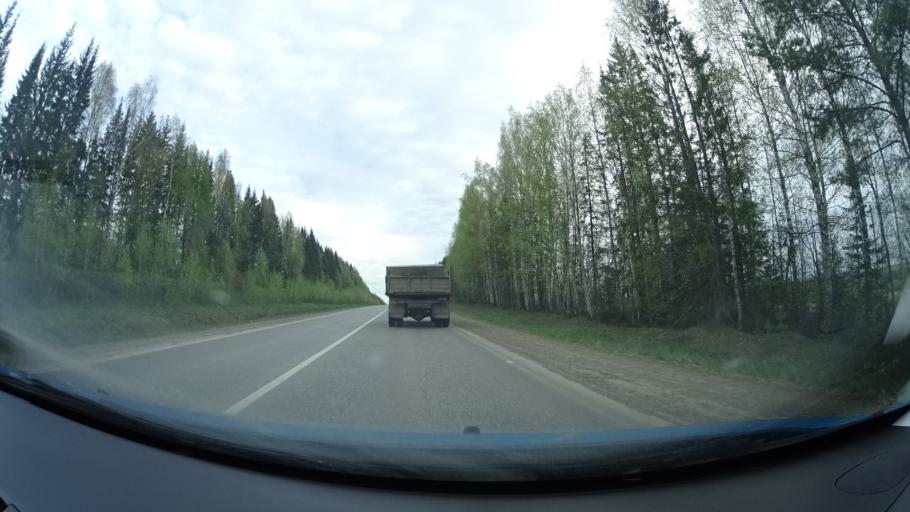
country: RU
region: Perm
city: Osa
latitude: 57.4080
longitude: 55.6232
